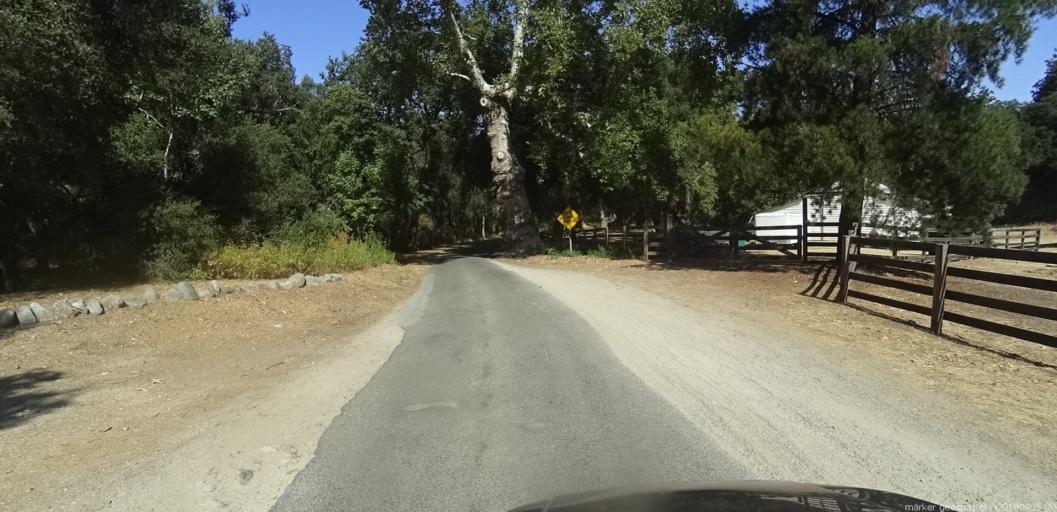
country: US
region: California
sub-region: Monterey County
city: Gonzales
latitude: 36.3763
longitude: -121.5912
